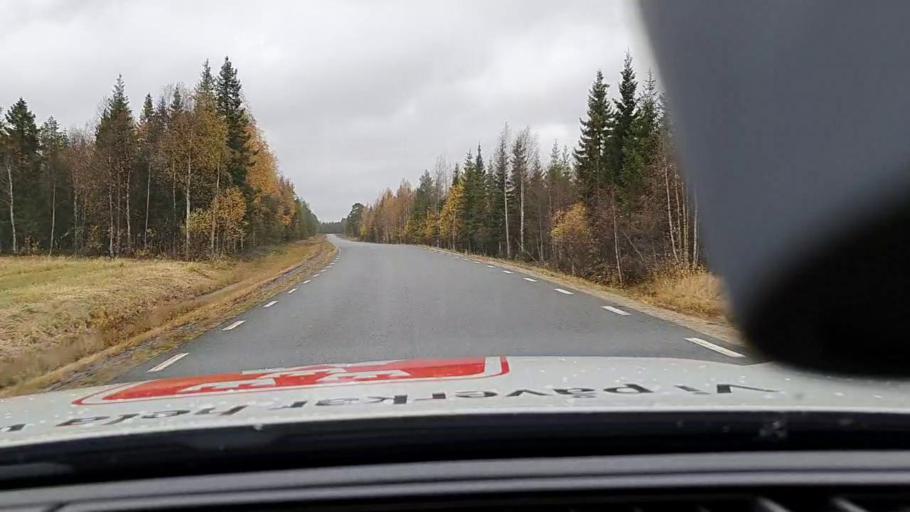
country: SE
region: Norrbotten
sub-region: Haparanda Kommun
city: Haparanda
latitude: 65.9340
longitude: 23.8139
